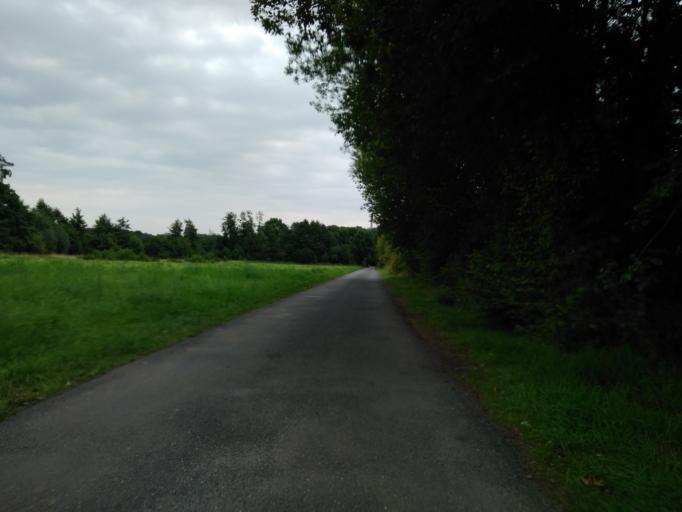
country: DE
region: North Rhine-Westphalia
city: Dorsten
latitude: 51.6270
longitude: 6.9731
